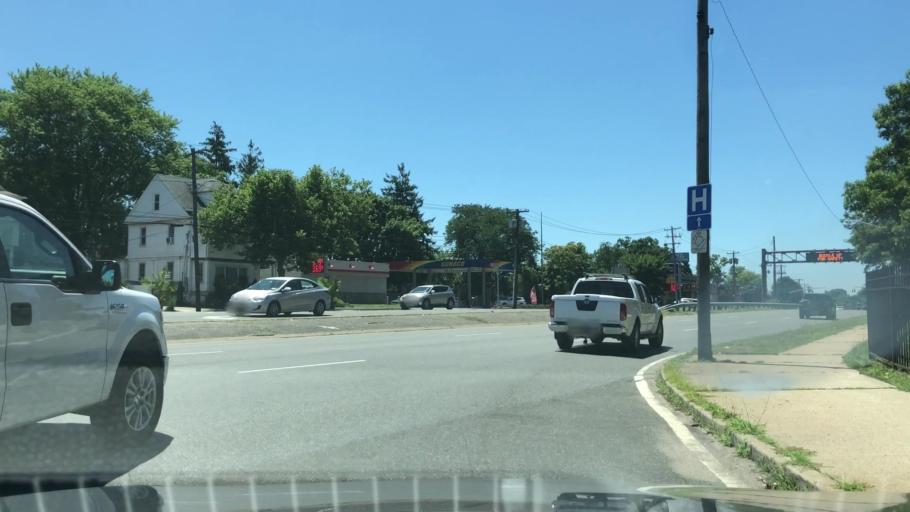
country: US
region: New York
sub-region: Nassau County
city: Hempstead
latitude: 40.6970
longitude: -73.6302
